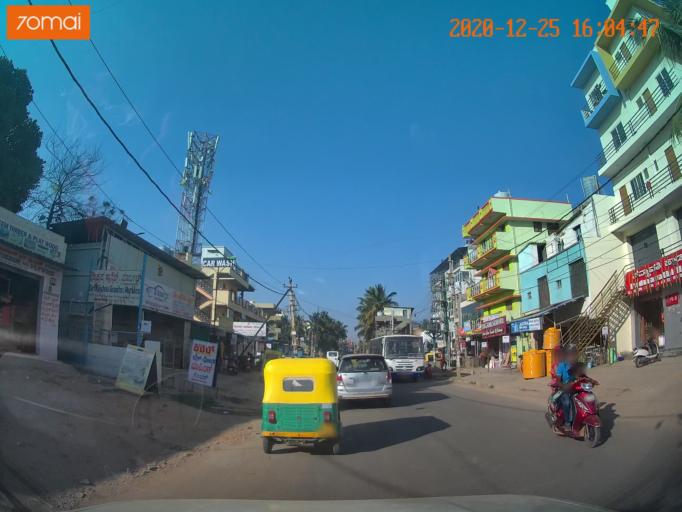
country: IN
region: Karnataka
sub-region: Bangalore Urban
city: Bangalore
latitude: 12.8873
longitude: 77.6255
